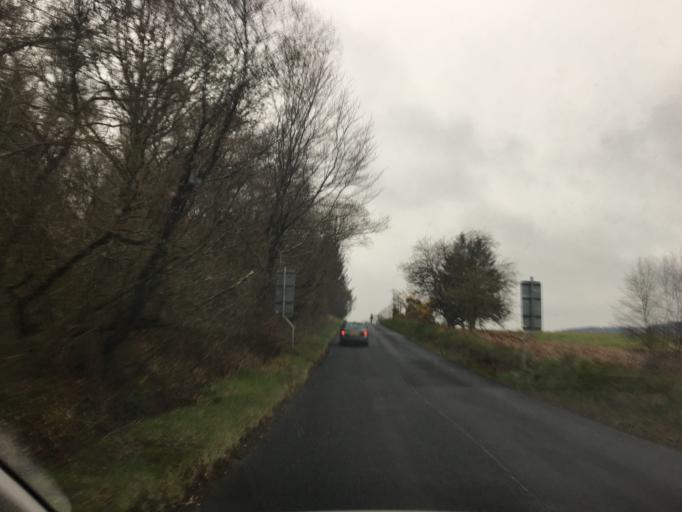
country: GB
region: Scotland
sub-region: North Ayrshire
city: Lamlash
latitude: 55.5441
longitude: -5.1314
